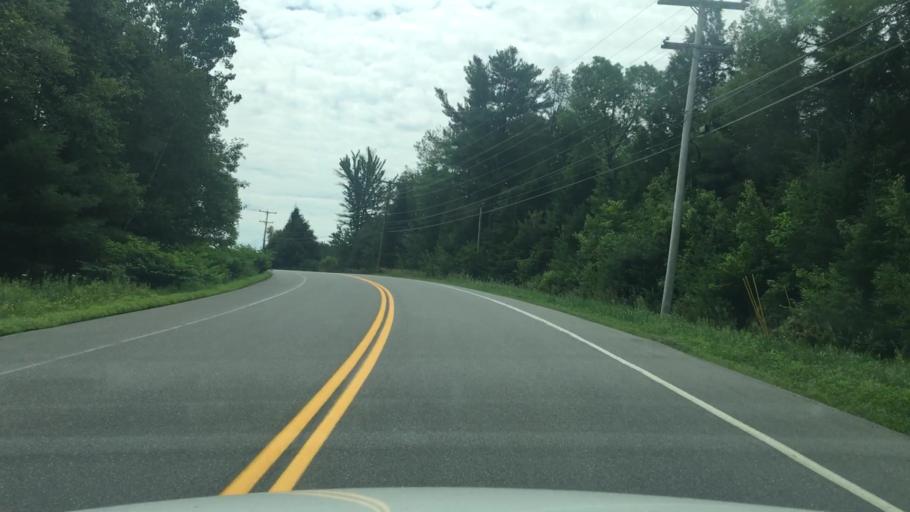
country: US
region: Maine
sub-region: Waldo County
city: Troy
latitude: 44.5684
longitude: -69.2791
